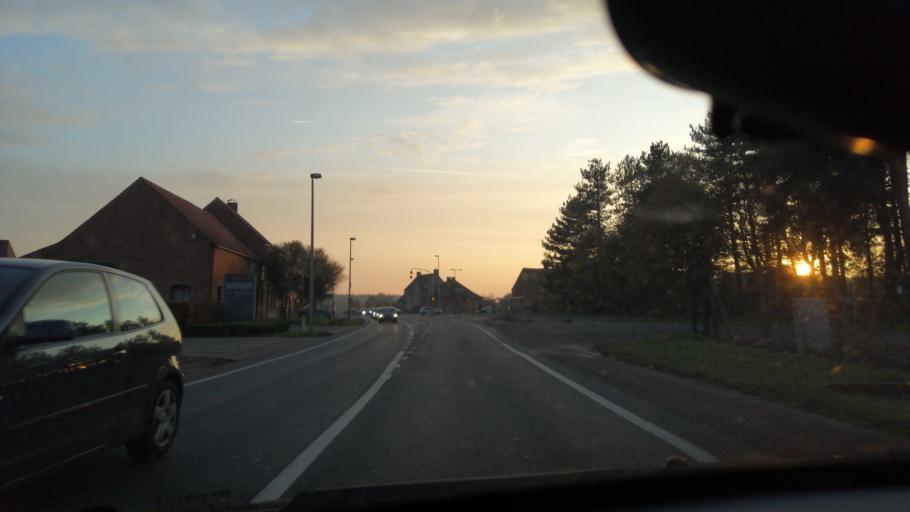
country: BE
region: Flanders
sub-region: Provincie Antwerpen
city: Lille
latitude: 51.2116
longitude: 4.8188
